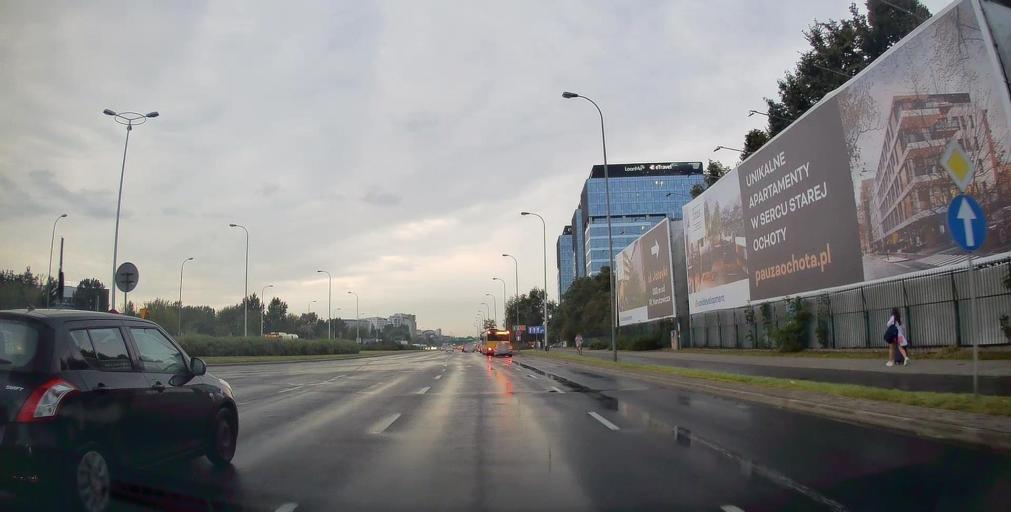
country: PL
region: Masovian Voivodeship
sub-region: Warszawa
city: Ursynow
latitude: 52.1548
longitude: 21.0461
